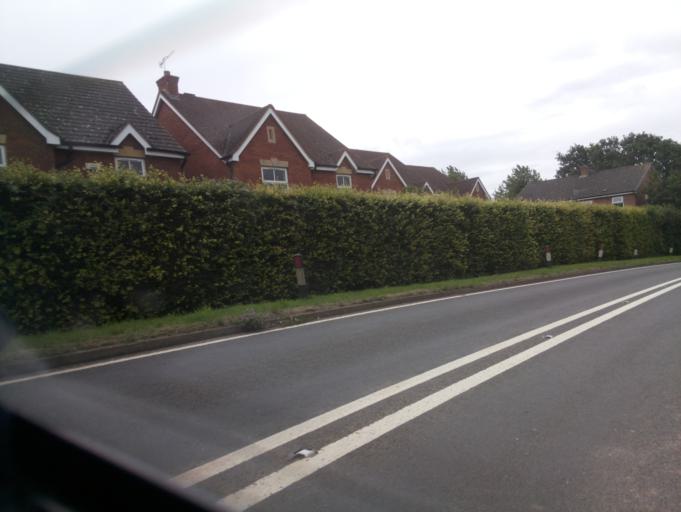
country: GB
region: England
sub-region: Worcestershire
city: Upton upon Severn
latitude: 52.0977
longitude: -2.2089
